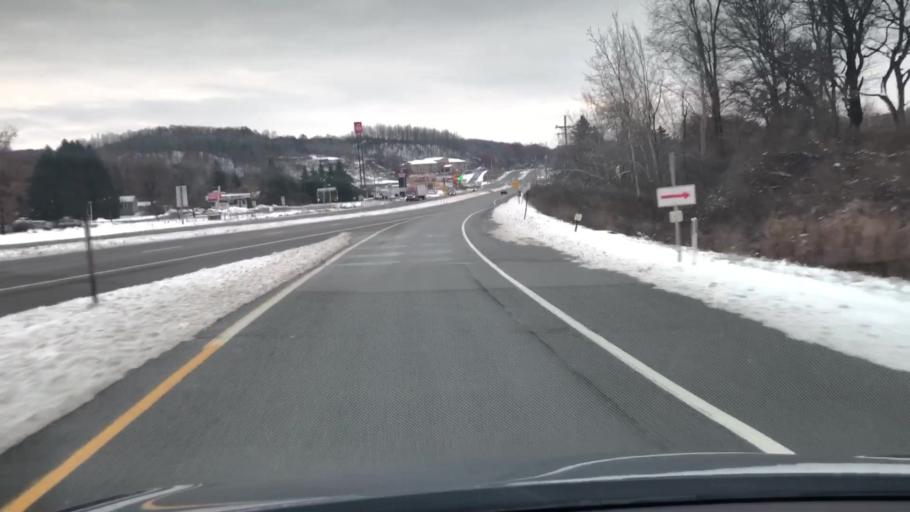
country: US
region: Pennsylvania
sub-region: Jefferson County
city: Falls Creek
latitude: 41.1451
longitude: -78.7882
